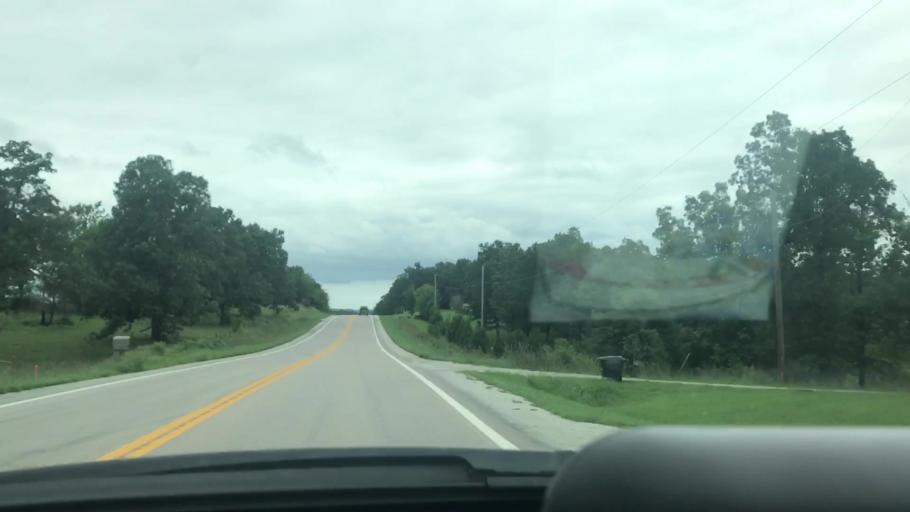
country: US
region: Missouri
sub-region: Dallas County
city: Buffalo
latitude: 37.7112
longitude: -93.1151
